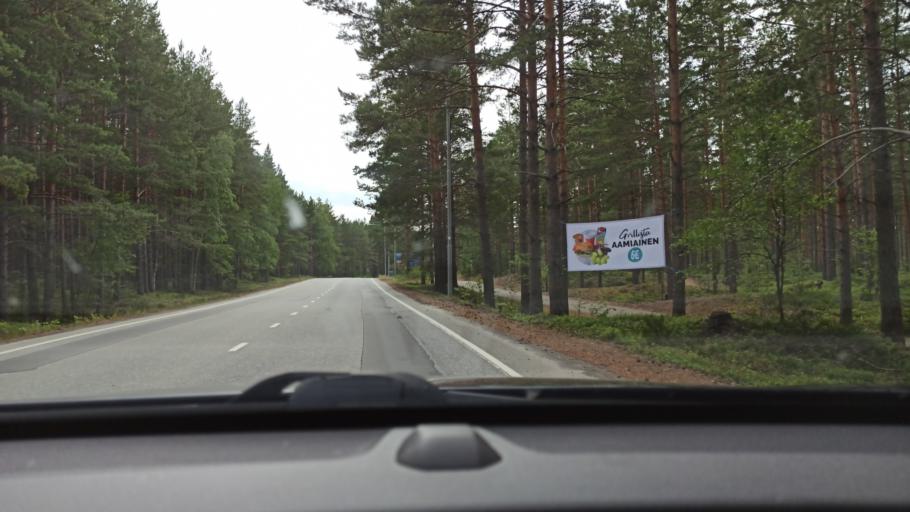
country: FI
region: Satakunta
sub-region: Pori
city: Luvia
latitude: 61.5727
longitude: 21.5372
